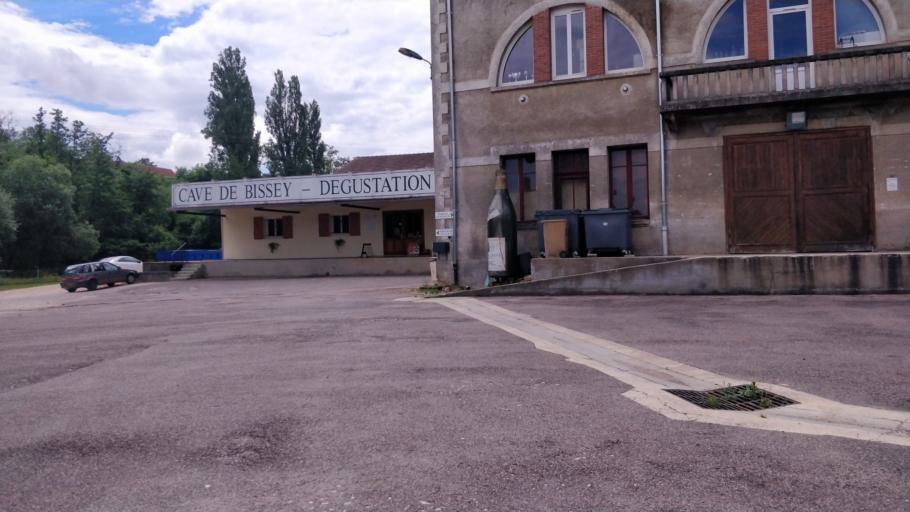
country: FR
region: Bourgogne
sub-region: Departement de Saone-et-Loire
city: Buxy
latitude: 46.7311
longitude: 4.6867
